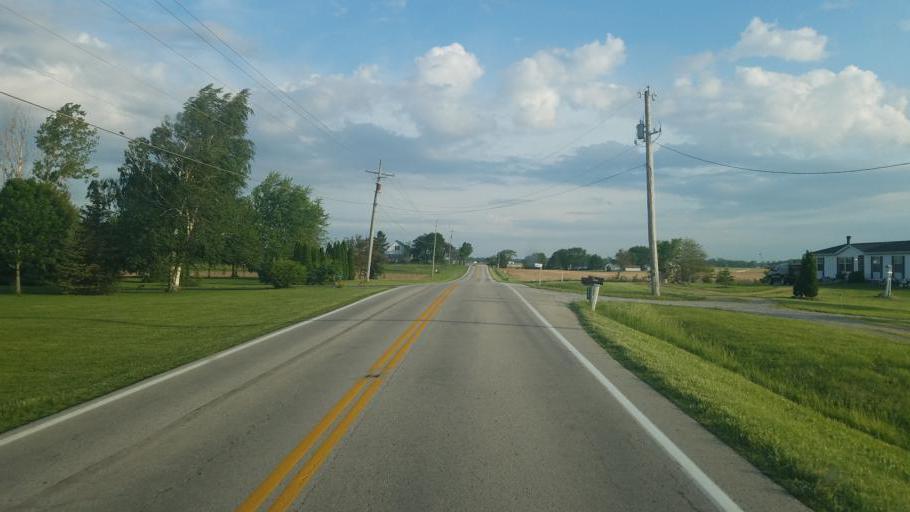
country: US
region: Ohio
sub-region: Clinton County
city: Sabina
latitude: 39.4386
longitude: -83.6360
